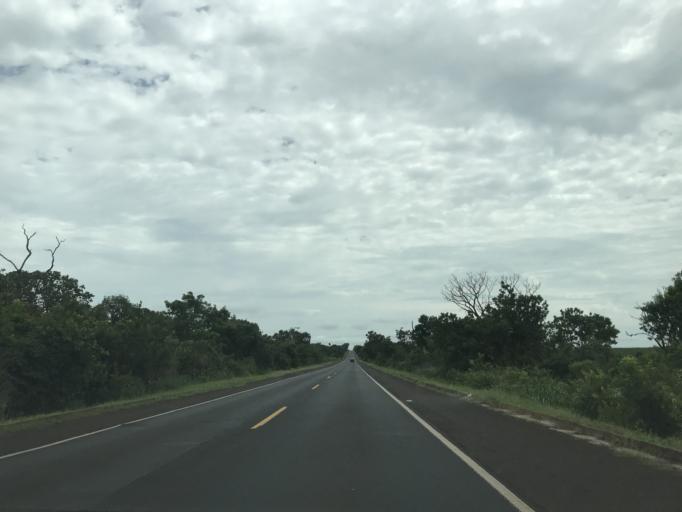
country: BR
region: Minas Gerais
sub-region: Frutal
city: Frutal
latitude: -19.9793
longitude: -49.0120
